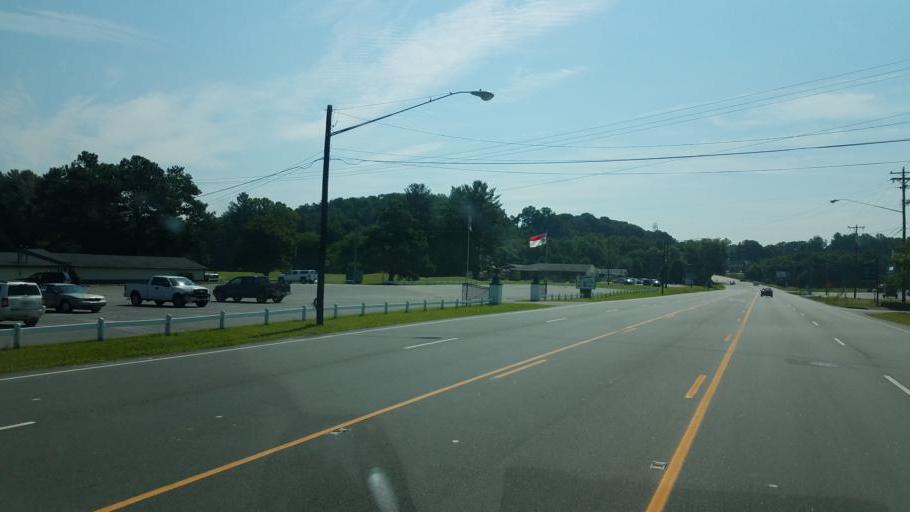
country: US
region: North Carolina
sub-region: Burke County
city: Morganton
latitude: 35.7514
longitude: -81.7106
